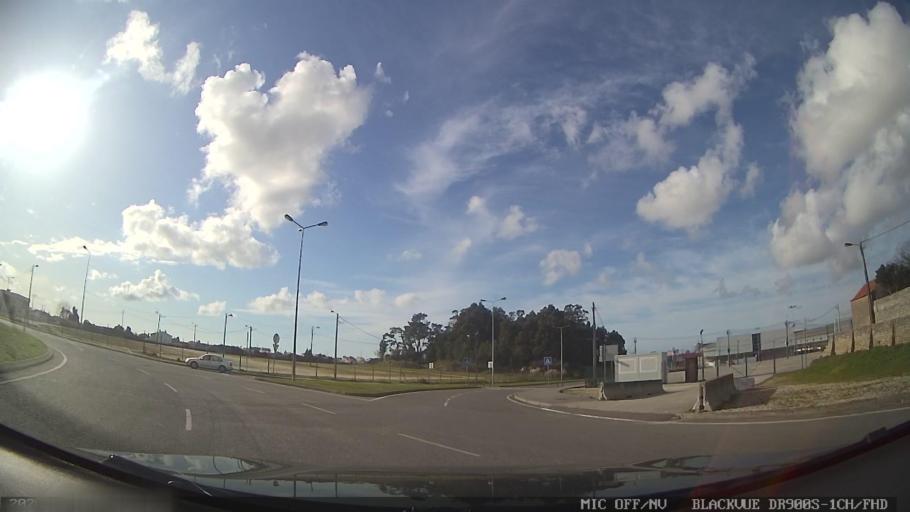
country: PT
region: Aveiro
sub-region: Aveiro
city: Aradas
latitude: 40.6320
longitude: -8.6297
